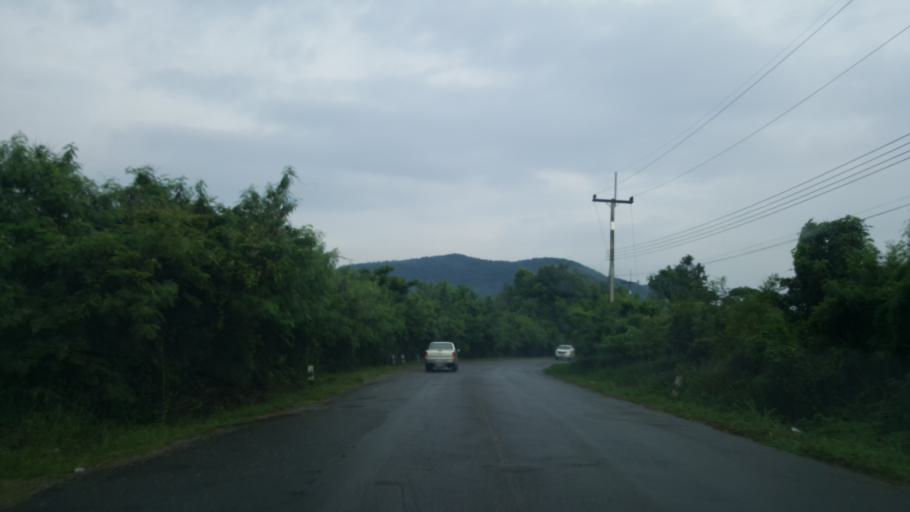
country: TH
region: Chon Buri
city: Sattahip
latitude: 12.7260
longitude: 100.9139
